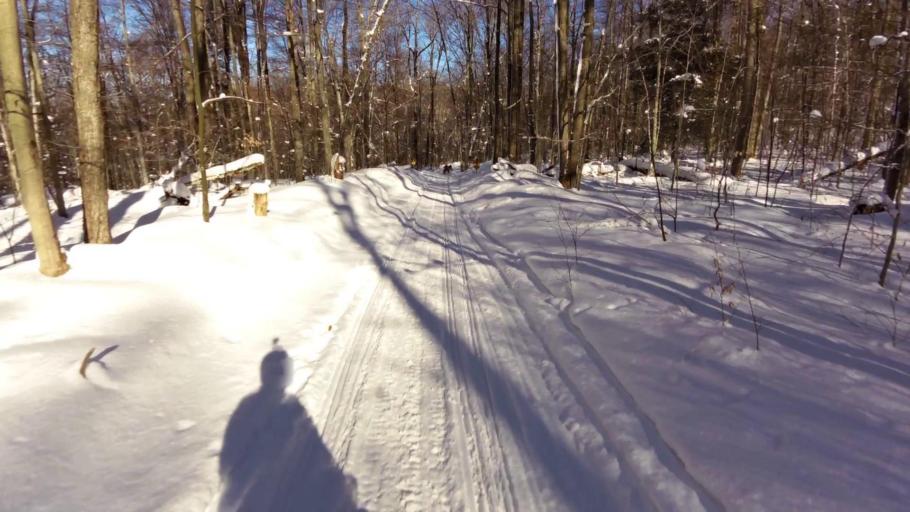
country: US
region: New York
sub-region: Cattaraugus County
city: Salamanca
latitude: 42.0395
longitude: -78.7822
